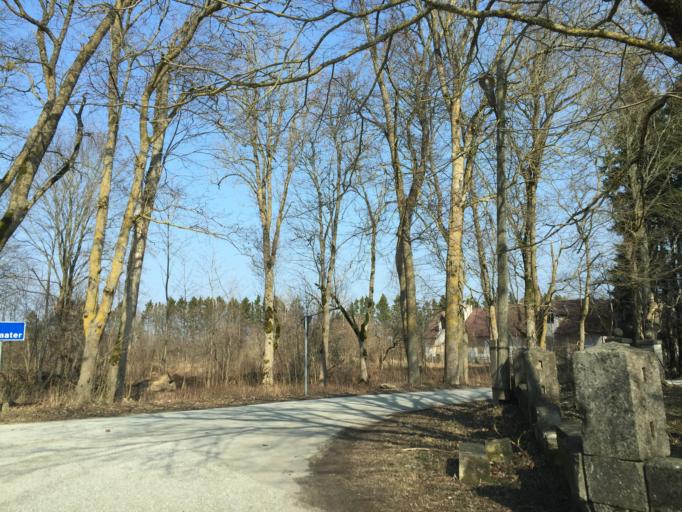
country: EE
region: Saare
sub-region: Kuressaare linn
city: Kuressaare
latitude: 58.3704
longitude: 22.6844
